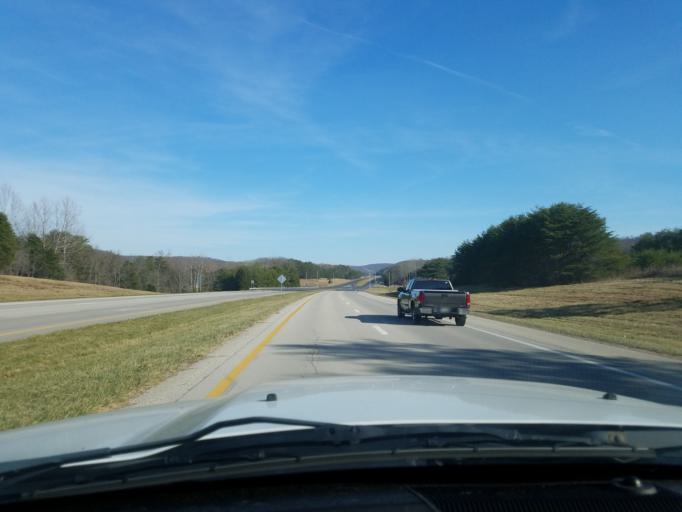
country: US
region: Ohio
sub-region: Adams County
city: Peebles
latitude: 38.9729
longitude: -83.3428
